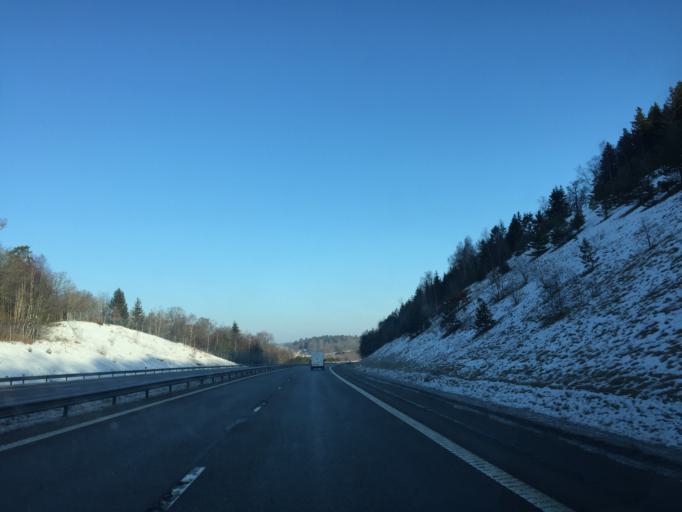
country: SE
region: Vaestra Goetaland
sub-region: Uddevalla Kommun
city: Ljungskile
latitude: 58.1957
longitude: 11.9078
